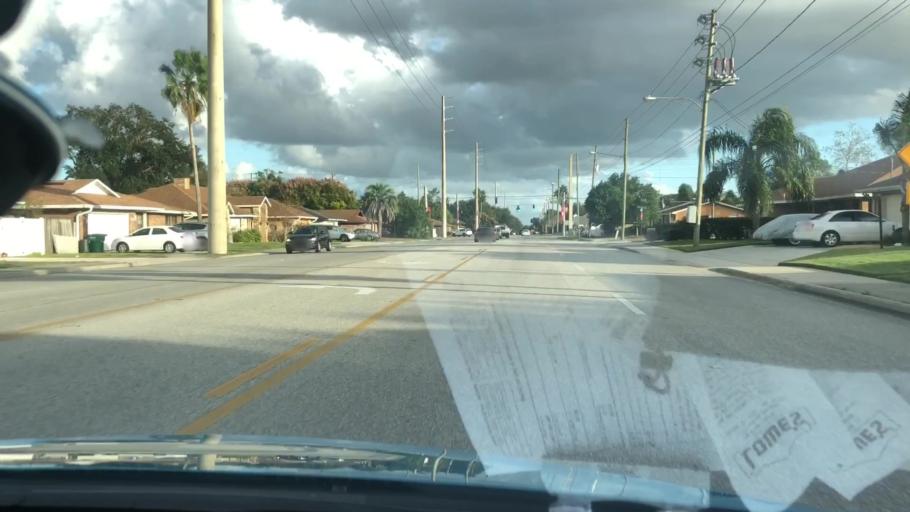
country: US
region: Florida
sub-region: Volusia County
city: Deltona
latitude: 28.9017
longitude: -81.2412
